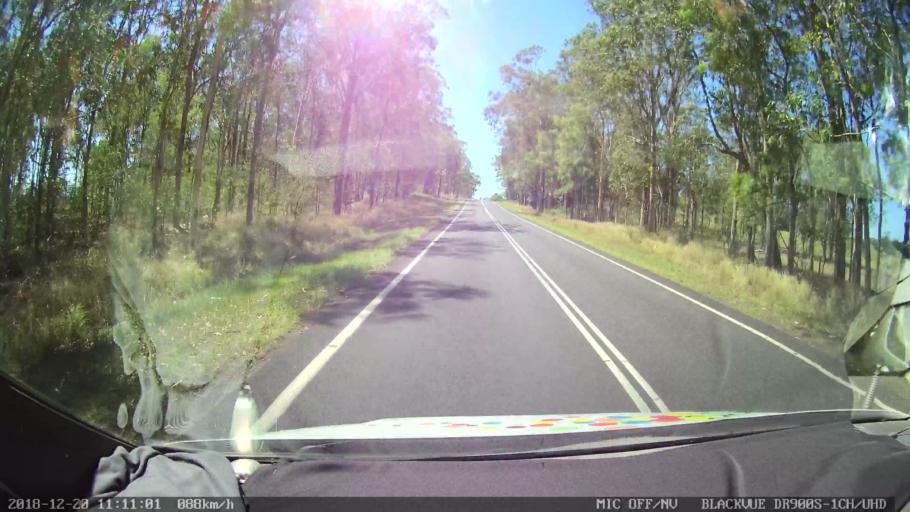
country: AU
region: New South Wales
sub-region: Richmond Valley
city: Casino
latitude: -28.9564
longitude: 153.0121
